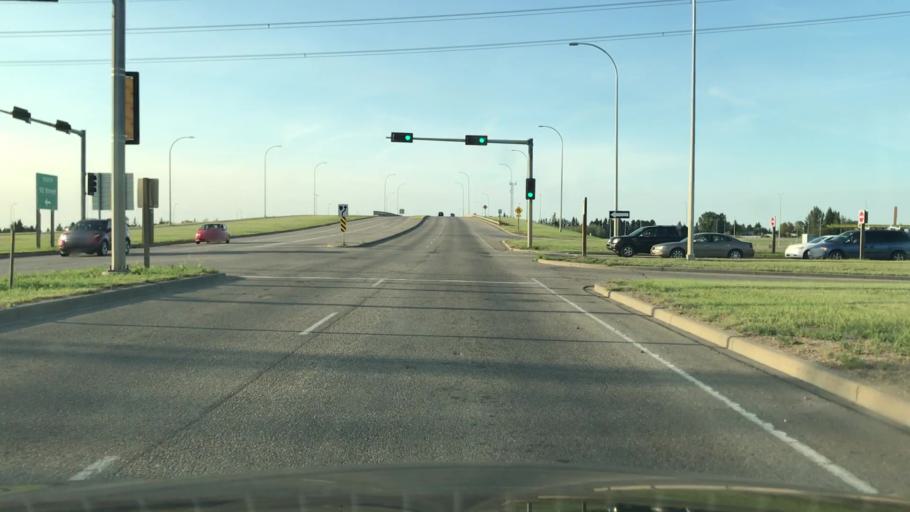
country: CA
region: Alberta
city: Beaumont
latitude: 53.4329
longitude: -113.4178
